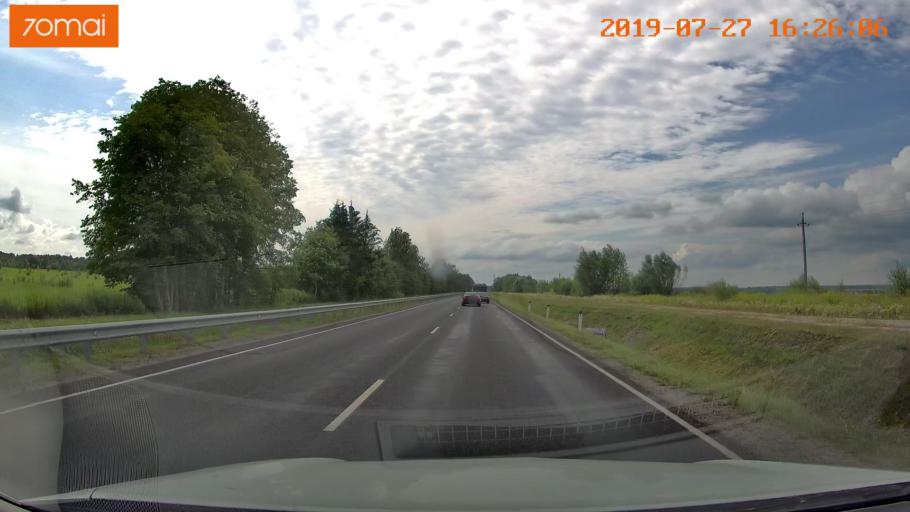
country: RU
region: Kaliningrad
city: Zheleznodorozhnyy
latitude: 54.6393
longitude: 21.4176
